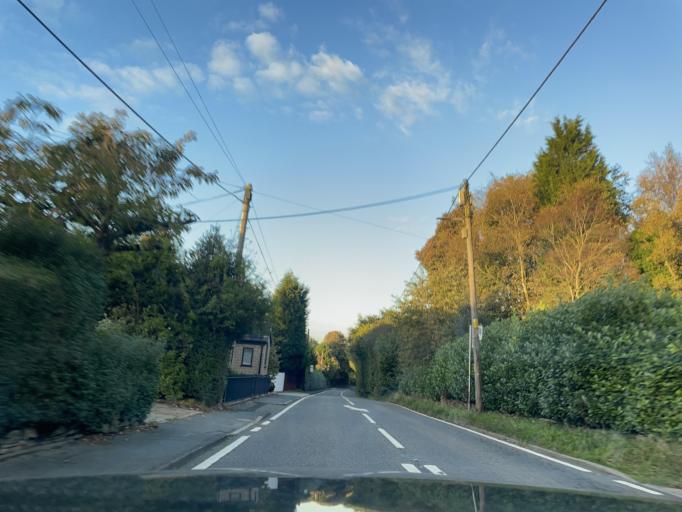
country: GB
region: England
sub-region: Borough of Stockport
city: Marple
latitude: 53.4225
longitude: -2.0287
